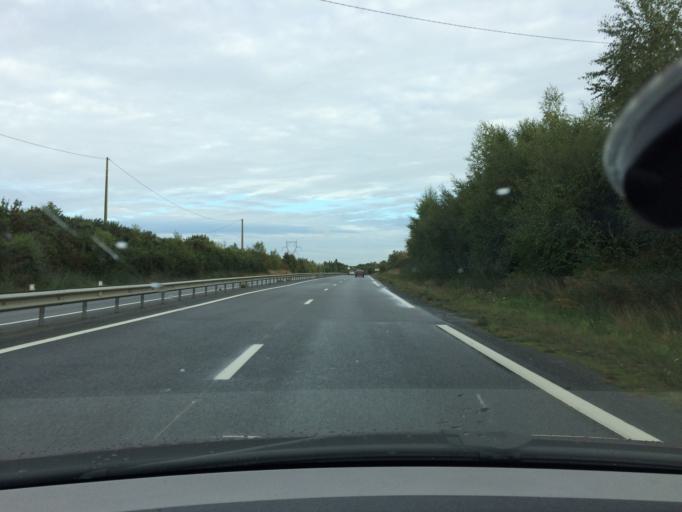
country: FR
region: Brittany
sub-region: Departement d'Ille-et-Vilaine
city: Janze
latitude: 47.9584
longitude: -1.5183
